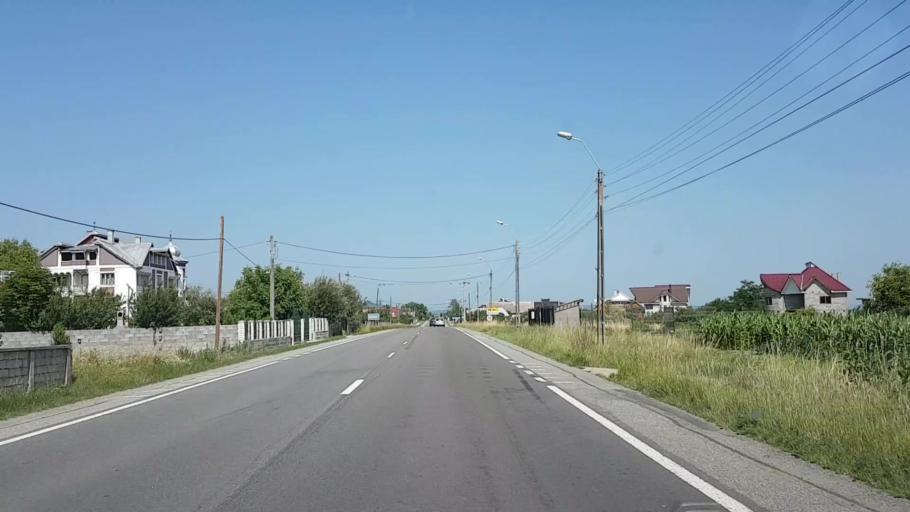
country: RO
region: Cluj
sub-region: Comuna Cusdrioara
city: Cusdrioara
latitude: 47.1750
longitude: 23.9382
